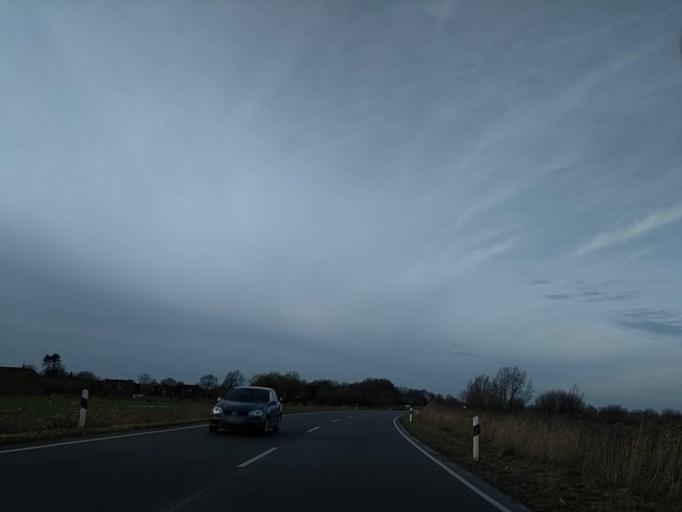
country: DE
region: Lower Saxony
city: Hinte
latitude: 53.3556
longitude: 7.1152
